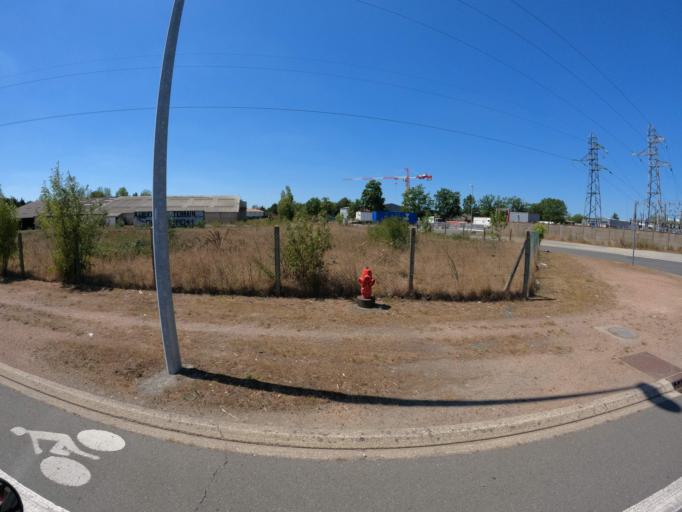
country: FR
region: Pays de la Loire
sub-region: Departement de la Vendee
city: Challans
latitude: 46.8485
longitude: -1.8594
